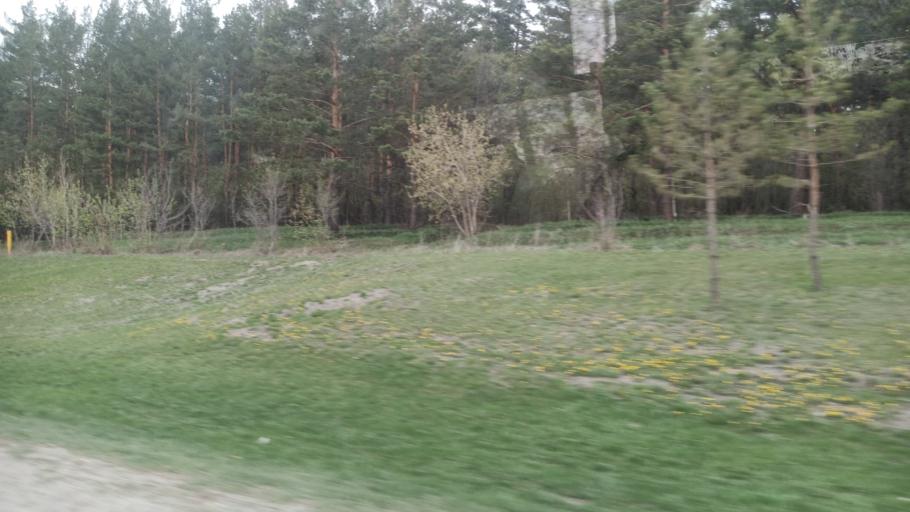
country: RU
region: Altai Krai
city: Yuzhnyy
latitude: 53.2629
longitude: 83.7044
